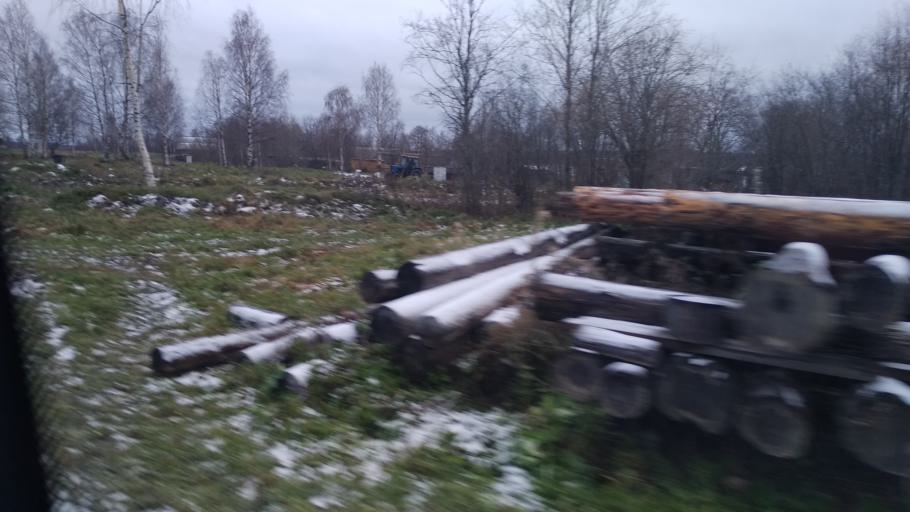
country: RU
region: Republic of Karelia
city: Shun'ga
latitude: 62.0848
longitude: 35.2060
